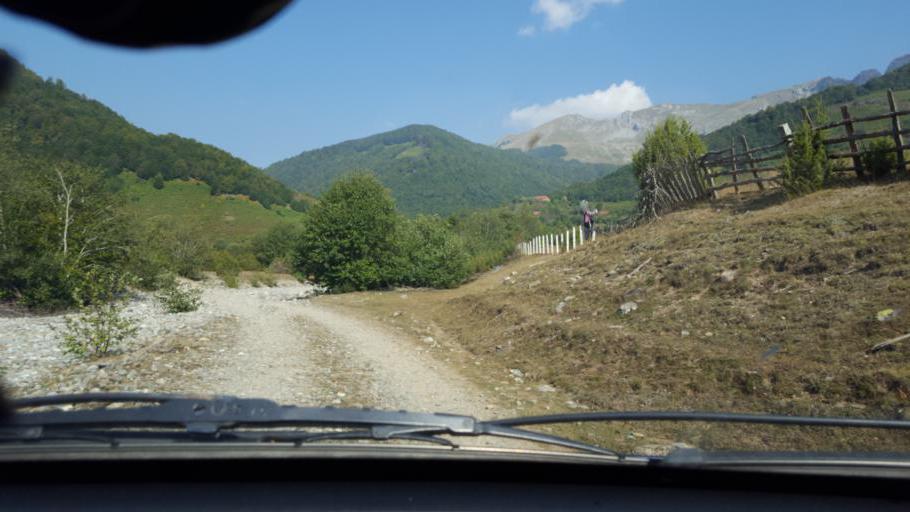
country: ME
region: Andrijevica
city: Andrijevica
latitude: 42.5971
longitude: 19.6597
